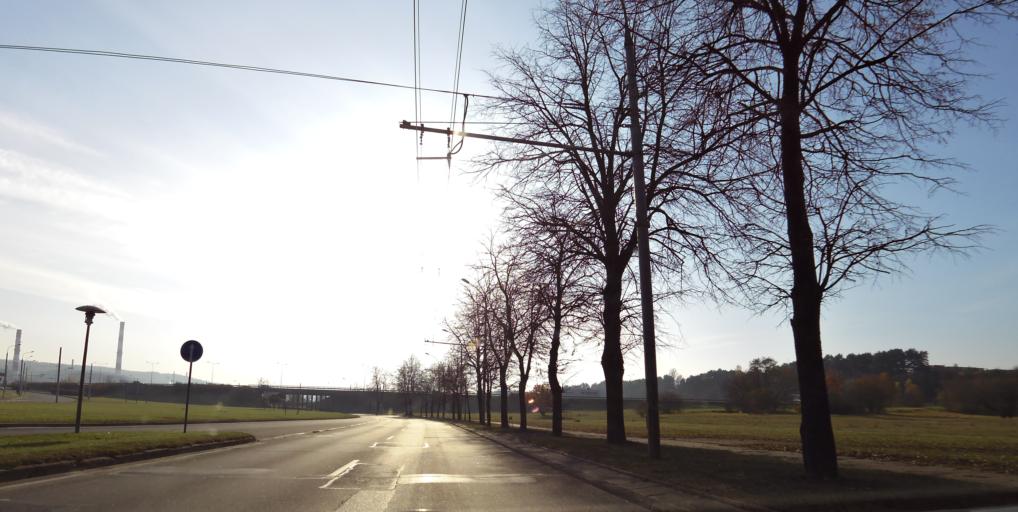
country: LT
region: Vilnius County
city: Lazdynai
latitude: 54.6736
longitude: 25.2225
